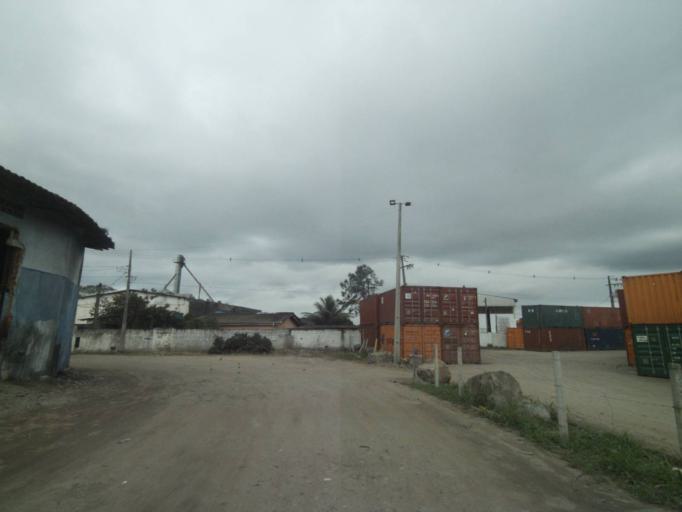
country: BR
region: Parana
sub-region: Paranagua
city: Paranagua
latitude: -25.5429
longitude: -48.5589
